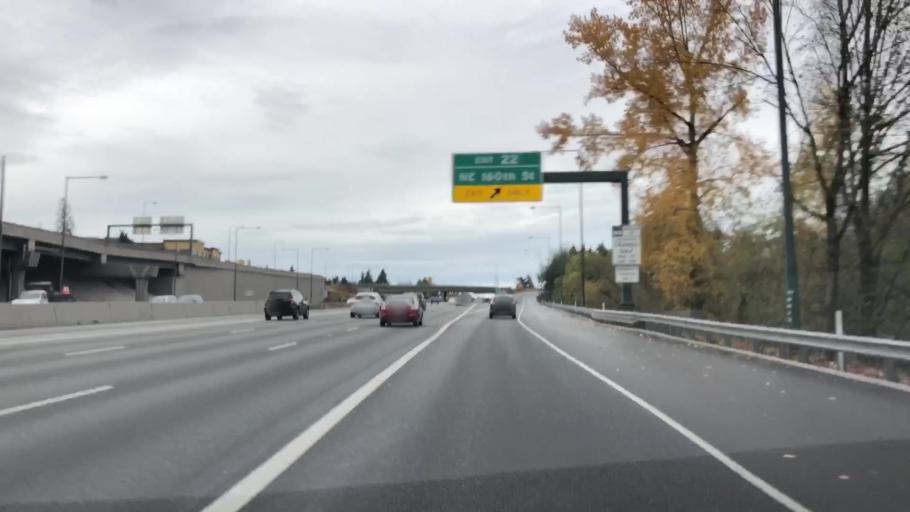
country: US
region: Washington
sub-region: King County
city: Kingsgate
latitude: 47.7468
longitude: -122.1874
